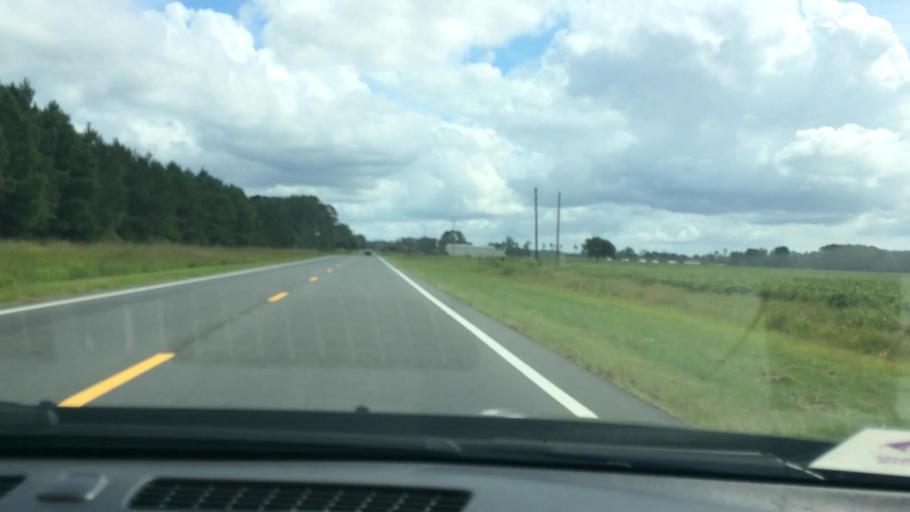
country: US
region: North Carolina
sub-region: Pitt County
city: Farmville
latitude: 35.5752
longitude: -77.5815
